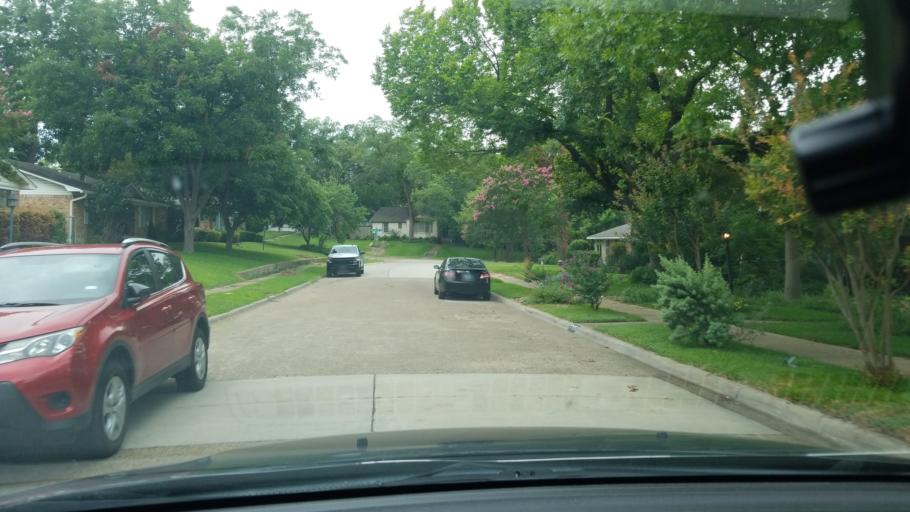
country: US
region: Texas
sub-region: Dallas County
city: Highland Park
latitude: 32.8122
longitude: -96.6945
